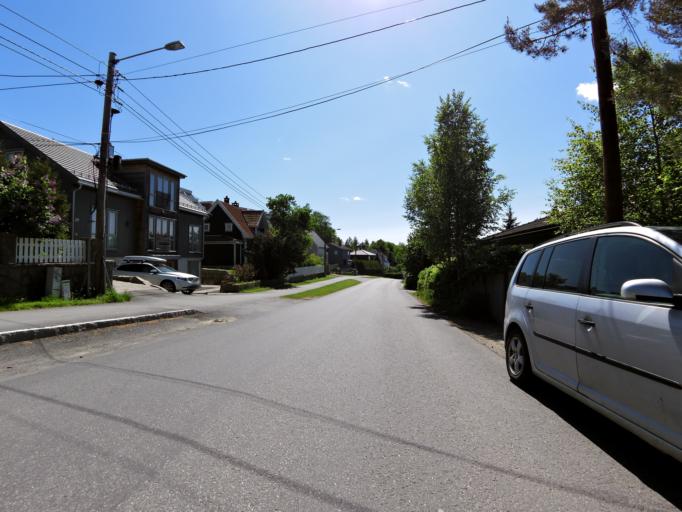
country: NO
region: Ostfold
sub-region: Fredrikstad
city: Fredrikstad
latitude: 59.2189
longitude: 10.9527
